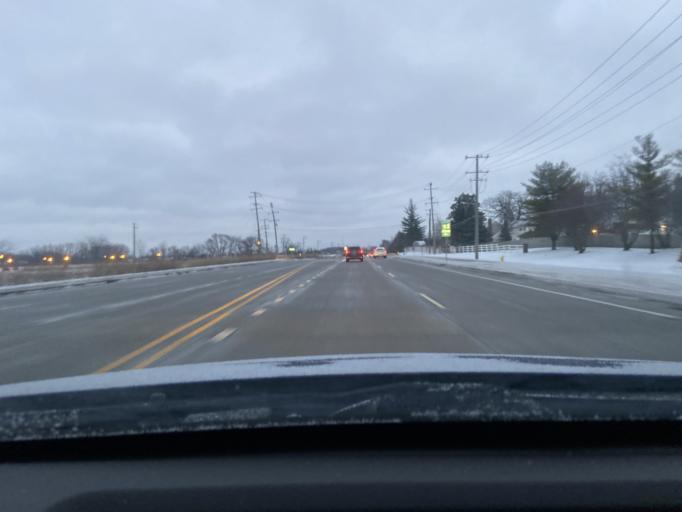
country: US
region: Illinois
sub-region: Lake County
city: Grayslake
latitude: 42.3570
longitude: -88.0525
